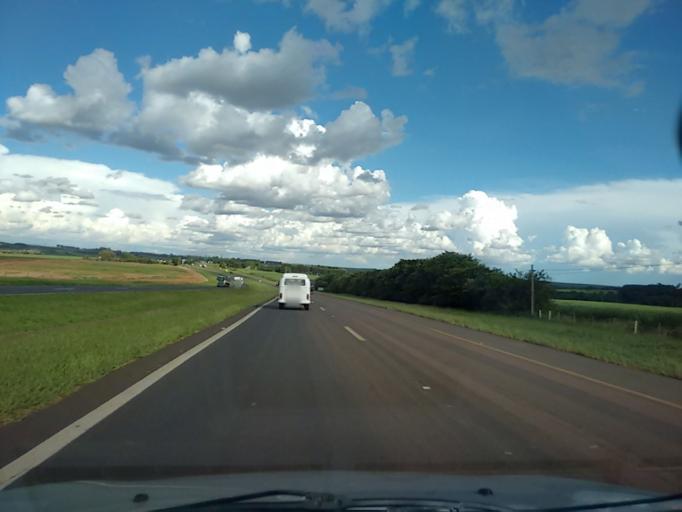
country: BR
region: Sao Paulo
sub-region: Ibate
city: Ibate
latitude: -21.9605
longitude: -47.9793
